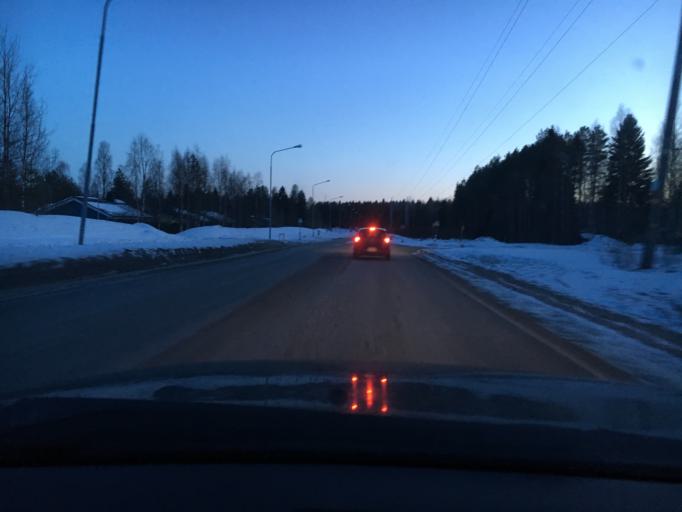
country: FI
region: Kainuu
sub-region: Kajaani
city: Kajaani
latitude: 64.2049
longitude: 27.7644
